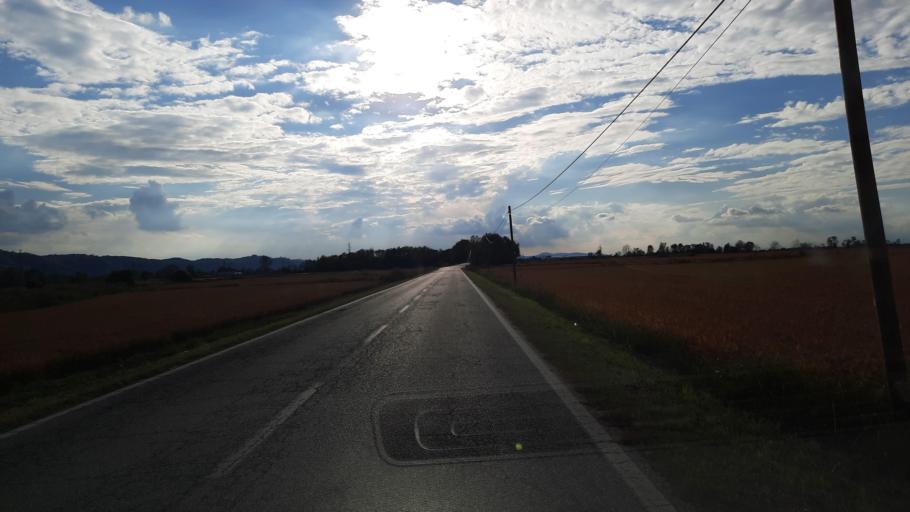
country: IT
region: Piedmont
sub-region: Provincia di Vercelli
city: Trino
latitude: 45.1934
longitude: 8.2645
